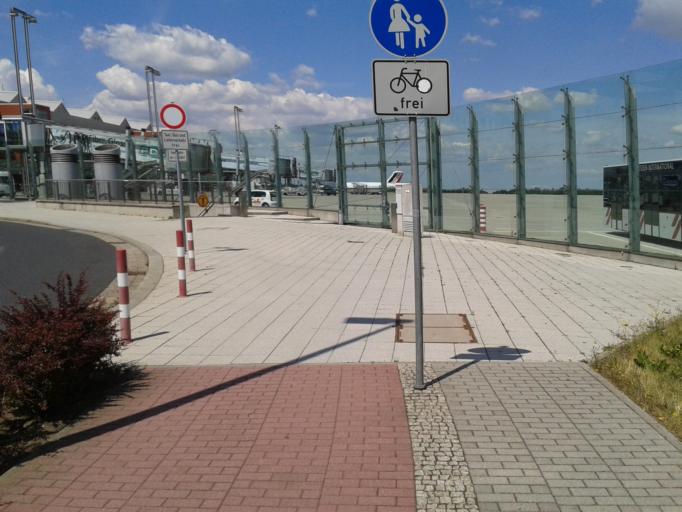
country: DE
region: Saxony
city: Albertstadt
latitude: 51.1252
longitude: 13.7677
